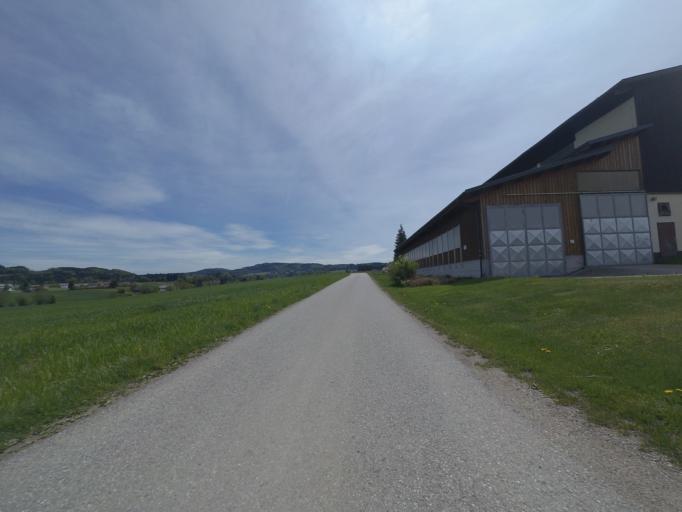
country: AT
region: Salzburg
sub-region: Politischer Bezirk Salzburg-Umgebung
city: Mattsee
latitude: 48.0022
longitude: 13.1124
